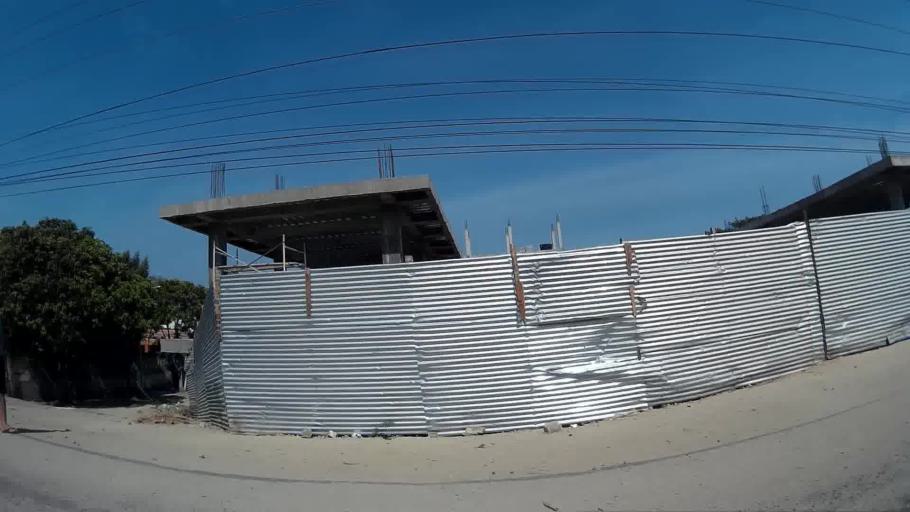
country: CO
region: Magdalena
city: Santa Marta
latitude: 11.1888
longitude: -74.2255
